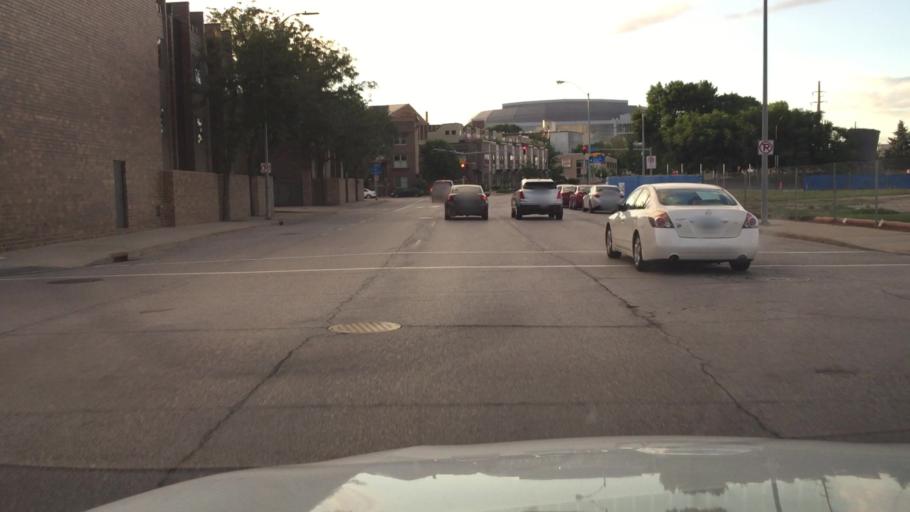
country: US
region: Iowa
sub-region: Polk County
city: Des Moines
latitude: 41.5879
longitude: -93.6201
